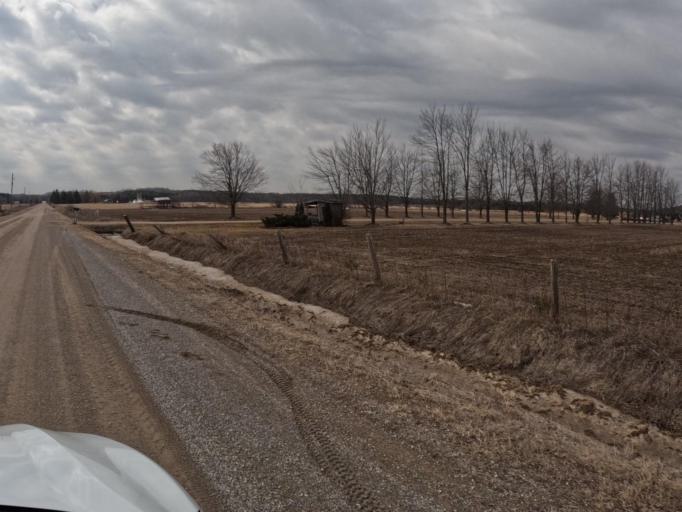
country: CA
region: Ontario
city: Orangeville
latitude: 43.9067
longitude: -80.2147
